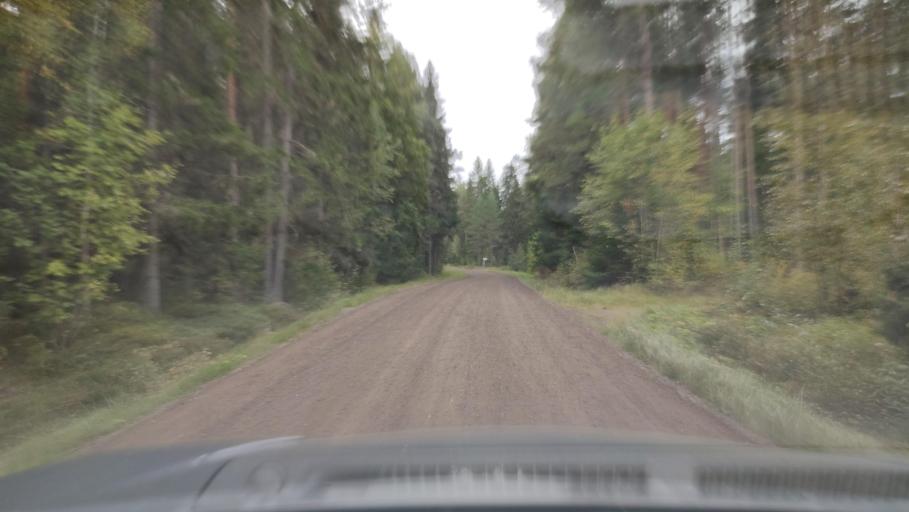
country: FI
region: Southern Ostrobothnia
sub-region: Suupohja
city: Karijoki
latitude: 62.2265
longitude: 21.5720
